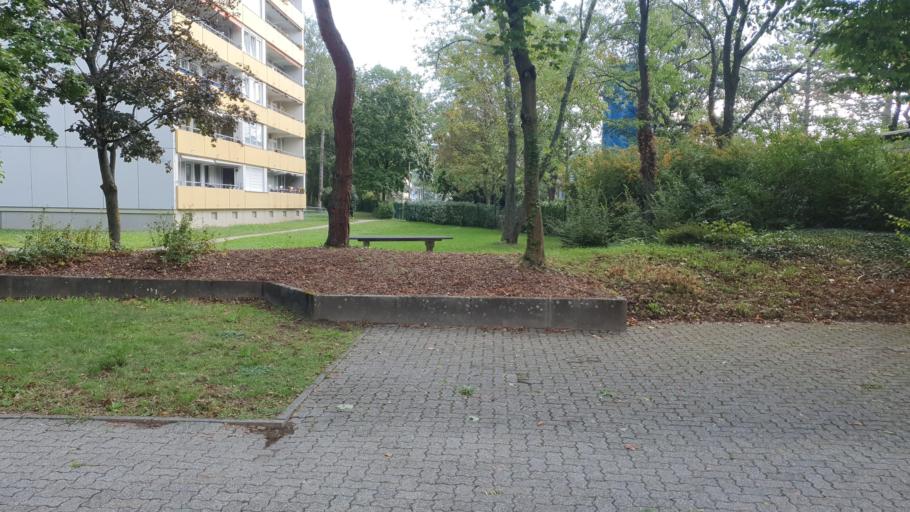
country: DE
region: Baden-Wuerttemberg
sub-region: Freiburg Region
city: Weil am Rhein
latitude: 47.5954
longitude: 7.6225
